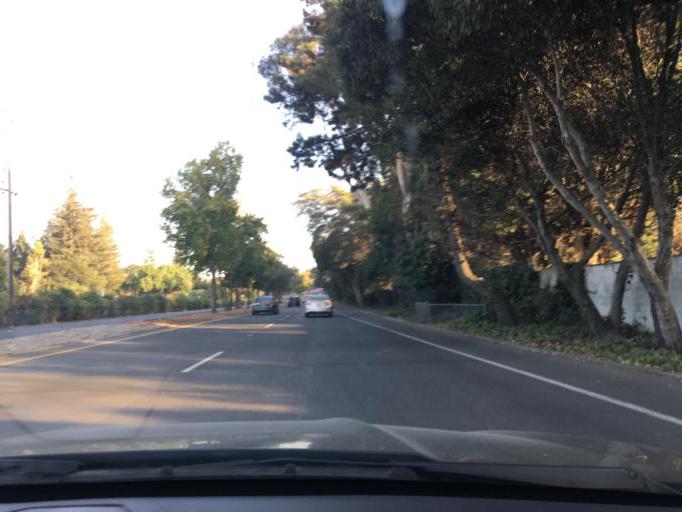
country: US
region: California
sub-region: Santa Clara County
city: Loyola
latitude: 37.3450
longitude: -122.0774
